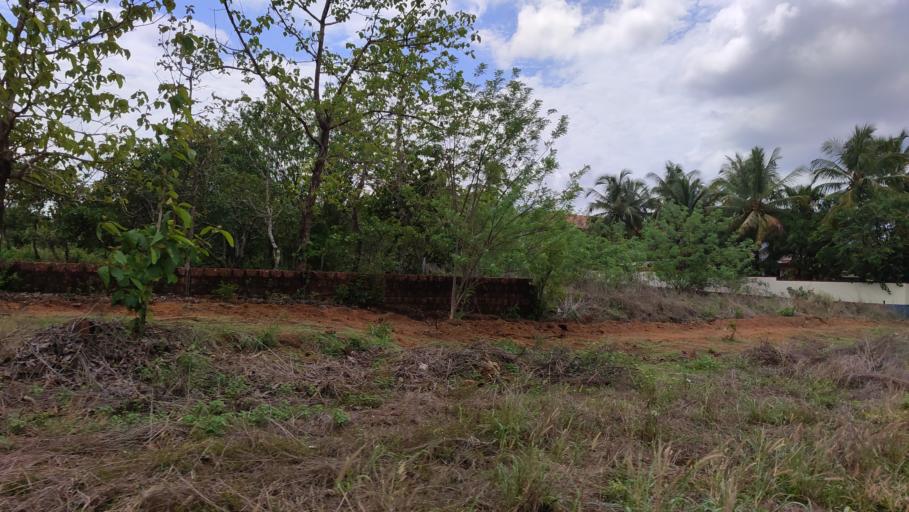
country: IN
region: Kerala
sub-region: Kasaragod District
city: Kannangad
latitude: 12.3989
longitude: 75.0972
